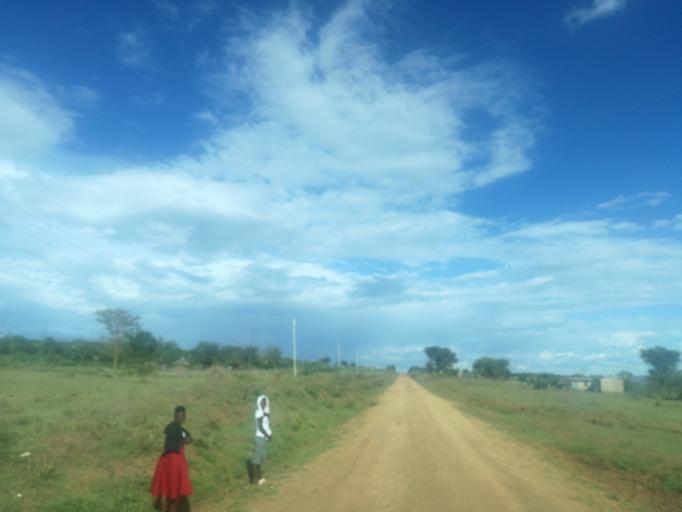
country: TZ
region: Mara
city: Issenye
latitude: -1.7545
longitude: 34.2561
